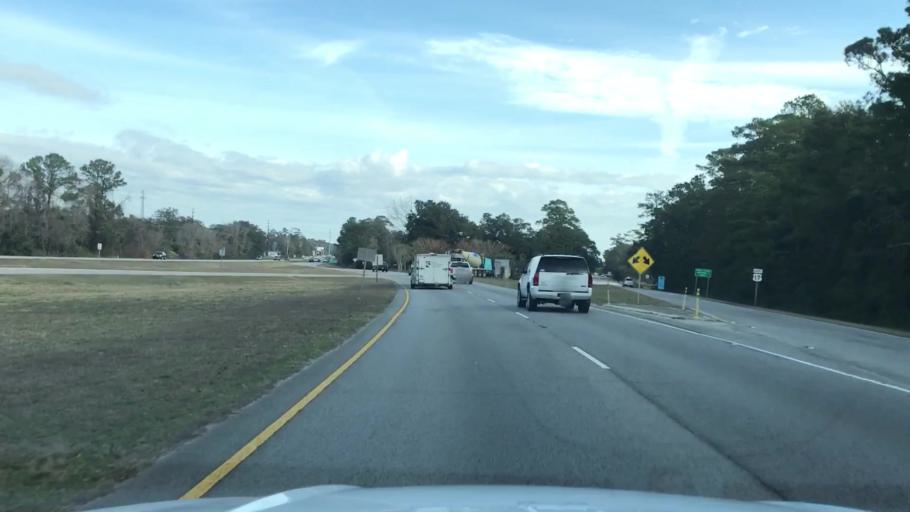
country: US
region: South Carolina
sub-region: Georgetown County
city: Murrells Inlet
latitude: 33.5277
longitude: -79.0629
